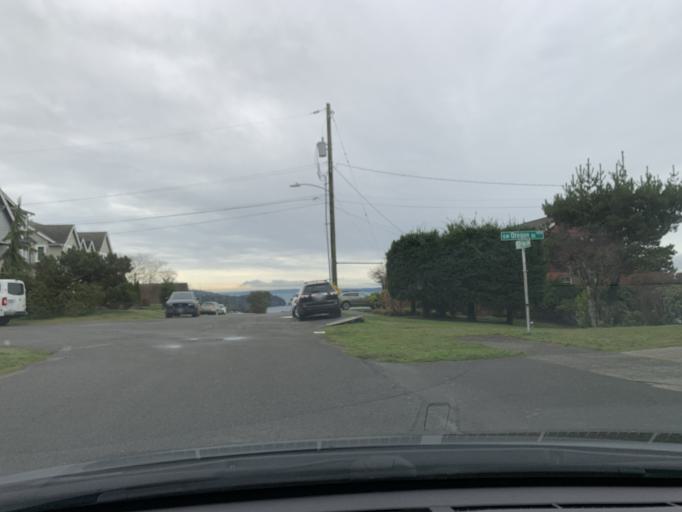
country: US
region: Washington
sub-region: King County
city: White Center
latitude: 47.5633
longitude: -122.3989
